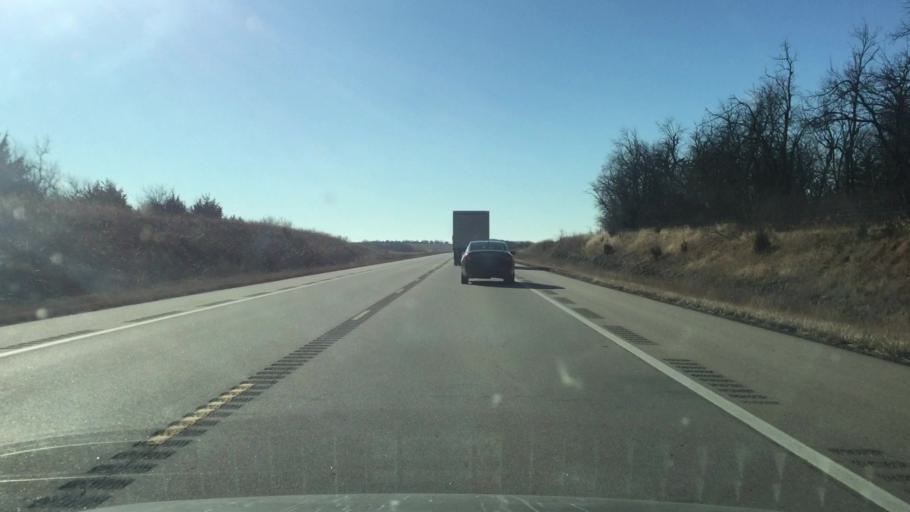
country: US
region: Kansas
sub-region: Allen County
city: Iola
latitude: 38.0325
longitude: -95.3806
